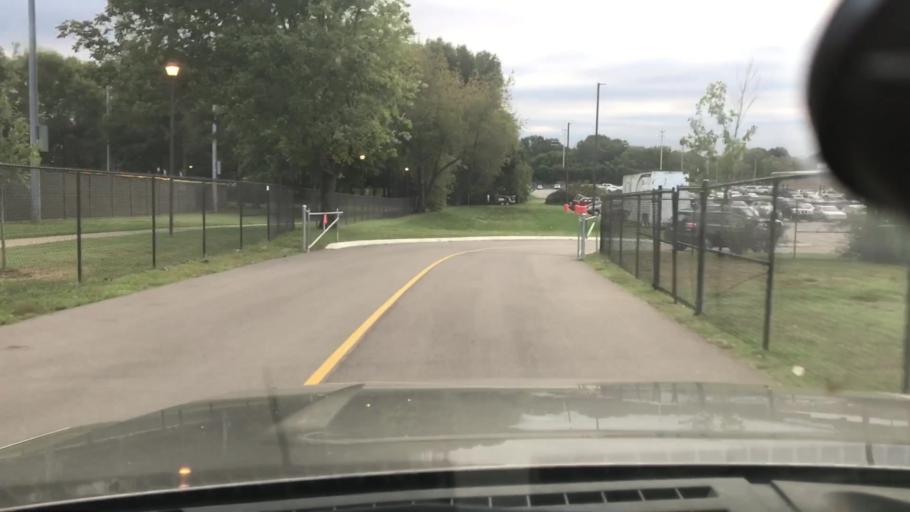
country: US
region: Tennessee
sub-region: Williamson County
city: Brentwood
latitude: 36.0182
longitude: -86.8177
